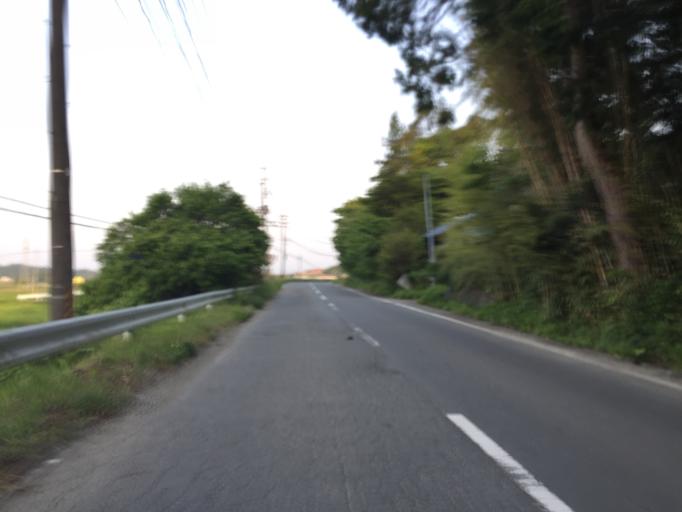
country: JP
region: Fukushima
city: Namie
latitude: 37.2714
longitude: 140.9889
